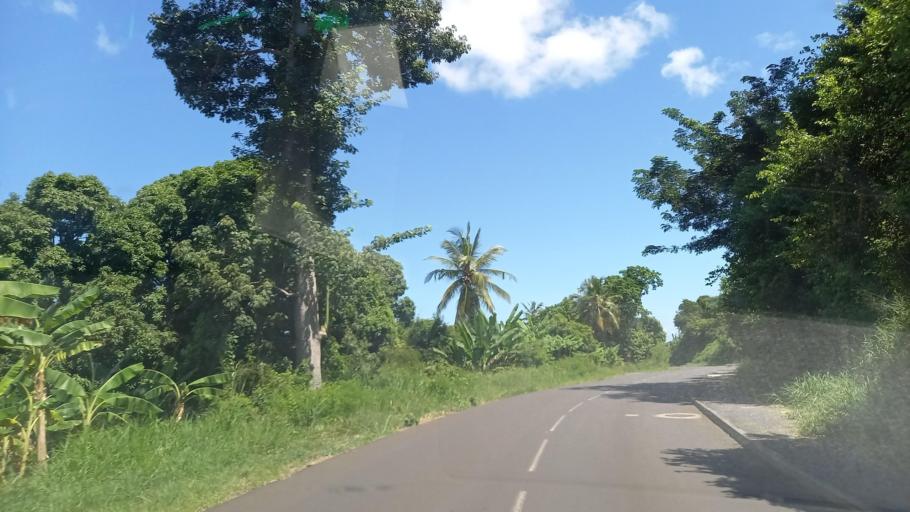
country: YT
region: Boueni
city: Boueni
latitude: -12.9241
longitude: 45.0962
